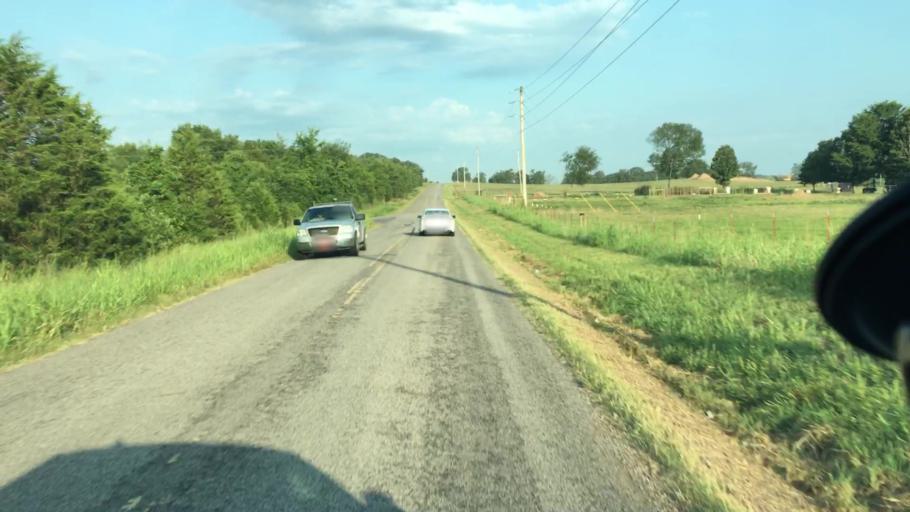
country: US
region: Arkansas
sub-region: Johnson County
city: Coal Hill
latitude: 35.3662
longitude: -93.6118
